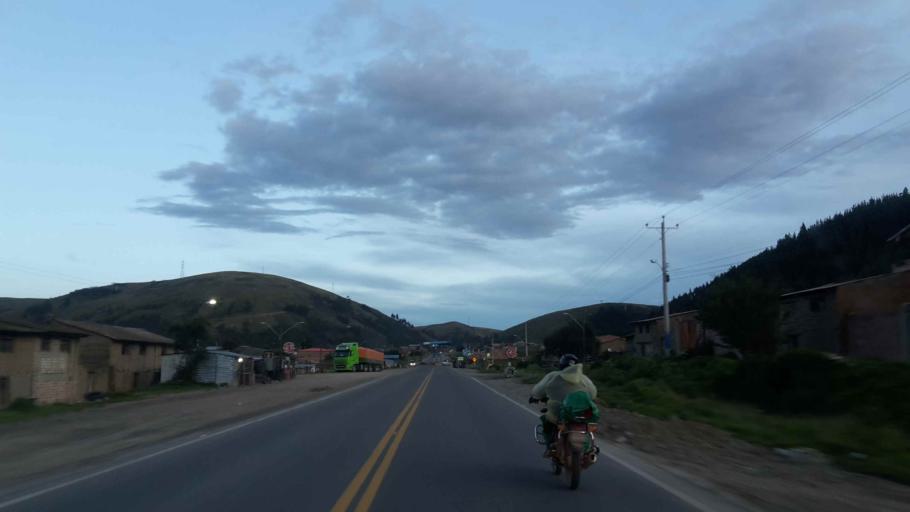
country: BO
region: Cochabamba
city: Colomi
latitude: -17.3646
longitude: -65.8406
